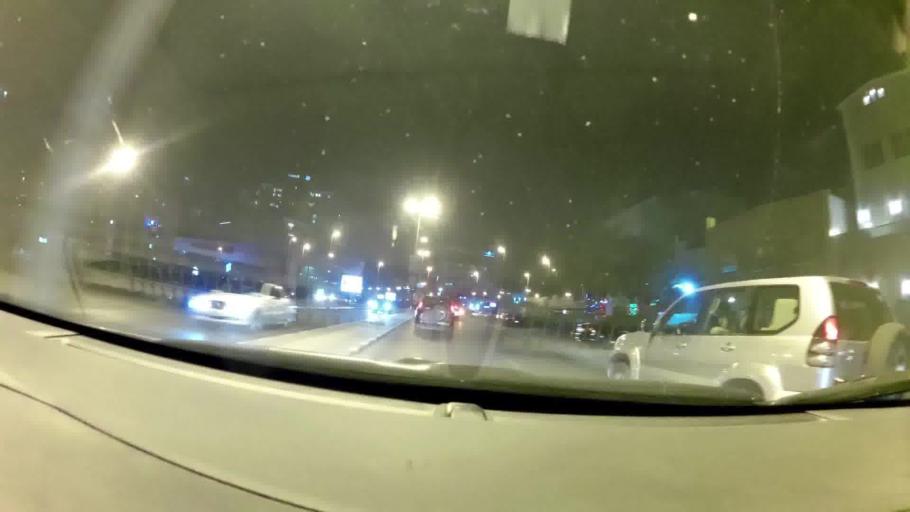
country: KW
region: Muhafazat Hawalli
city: As Salimiyah
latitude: 29.3420
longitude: 48.0830
